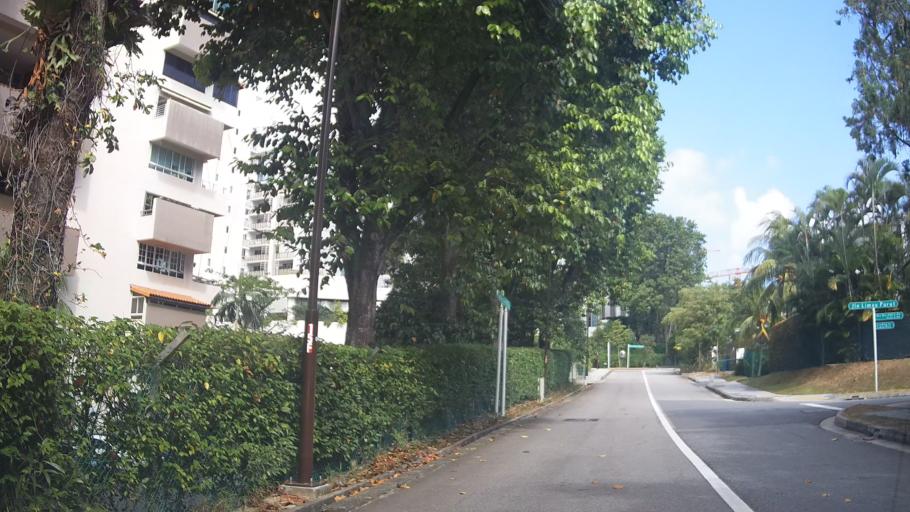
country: SG
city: Singapore
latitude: 1.3225
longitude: 103.9462
